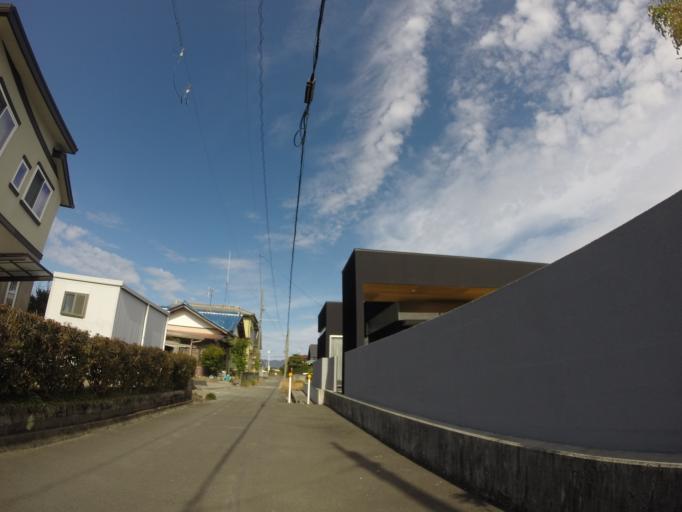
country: JP
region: Shizuoka
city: Fujieda
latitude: 34.8299
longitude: 138.2905
